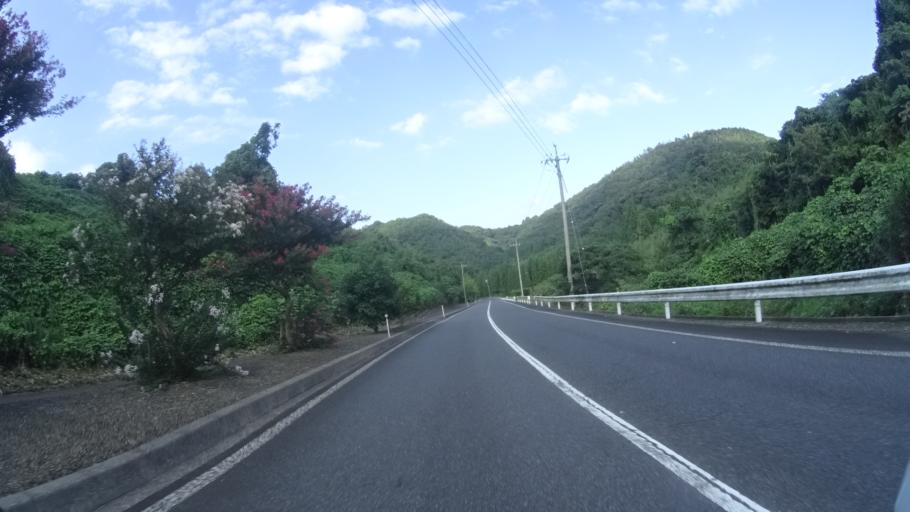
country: JP
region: Tottori
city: Kurayoshi
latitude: 35.4899
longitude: 133.8987
